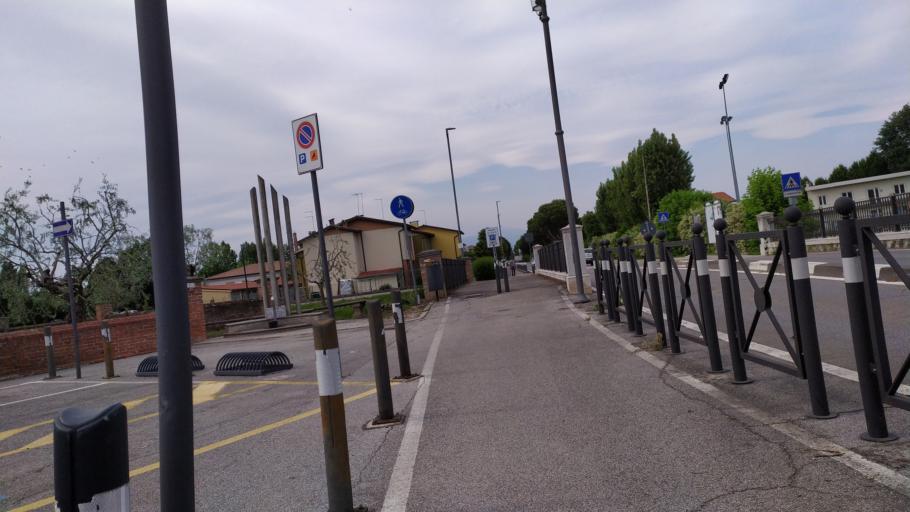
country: IT
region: Veneto
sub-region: Provincia di Padova
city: Villa del Conte
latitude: 45.5877
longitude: 11.8584
